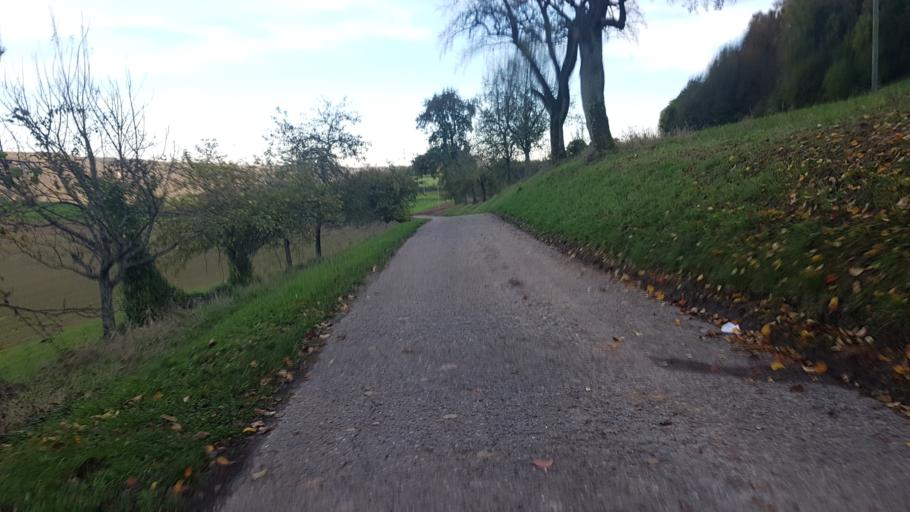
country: DE
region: Baden-Wuerttemberg
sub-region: Karlsruhe Region
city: Neckarzimmern
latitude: 49.3154
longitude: 9.1235
